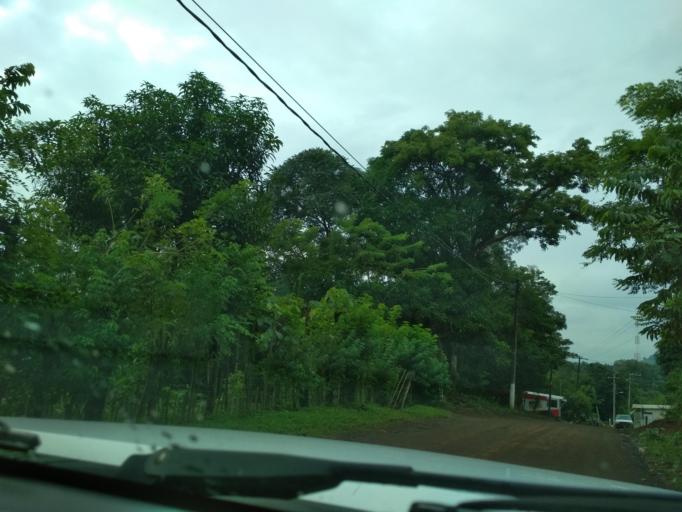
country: MX
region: Veracruz
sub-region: San Andres Tuxtla
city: Cerro las Iguanas
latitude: 18.4145
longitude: -95.1974
